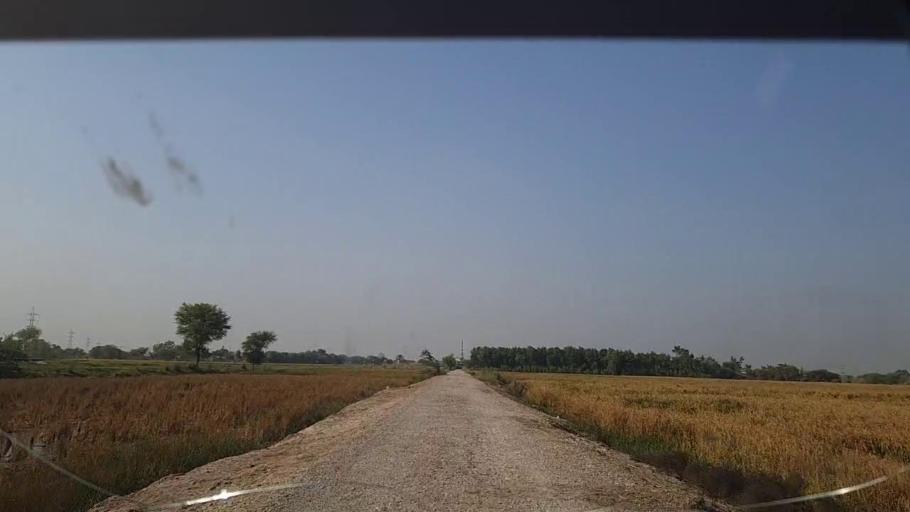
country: PK
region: Sindh
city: Shikarpur
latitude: 28.1178
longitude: 68.5731
